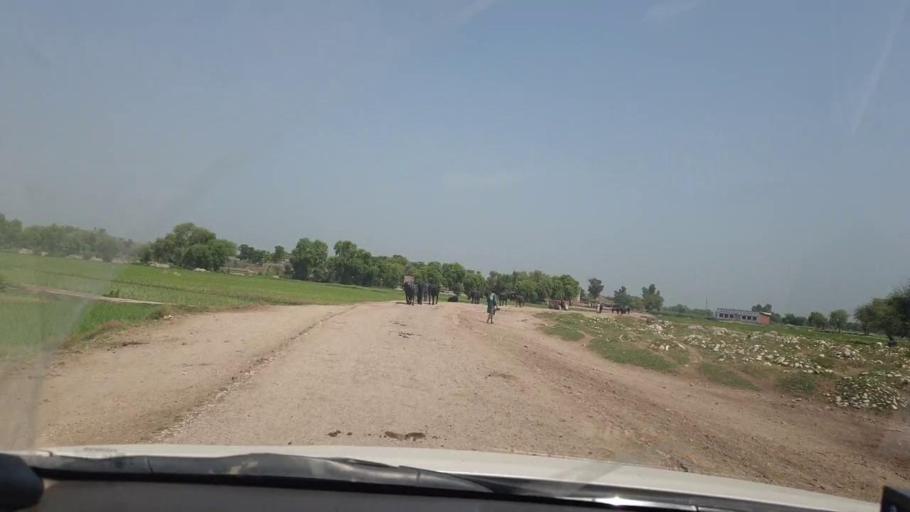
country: PK
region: Sindh
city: Chak
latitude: 27.8786
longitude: 68.7823
